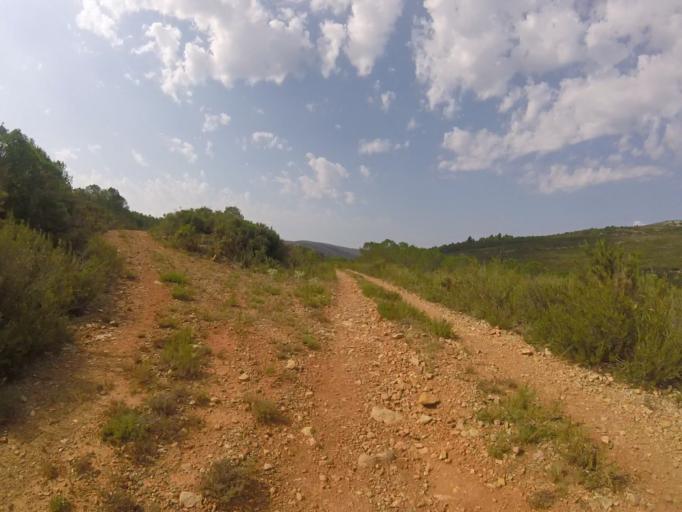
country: ES
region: Valencia
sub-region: Provincia de Castello
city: Alcala de Xivert
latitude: 40.3479
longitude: 0.1983
